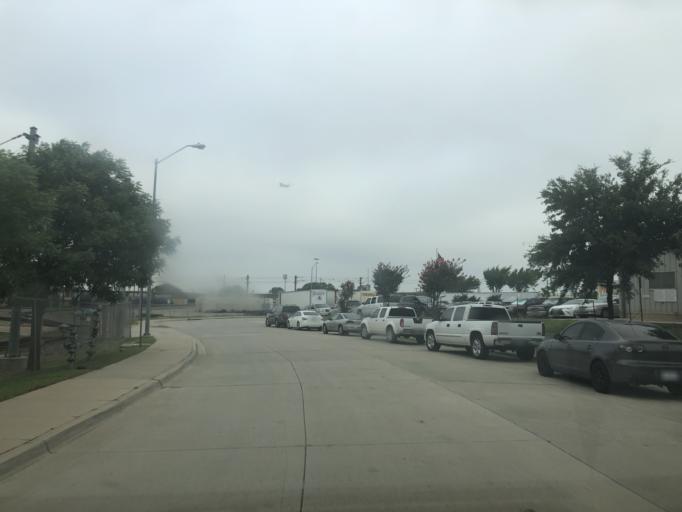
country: US
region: Texas
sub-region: Dallas County
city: Farmers Branch
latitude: 32.8708
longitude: -96.8789
